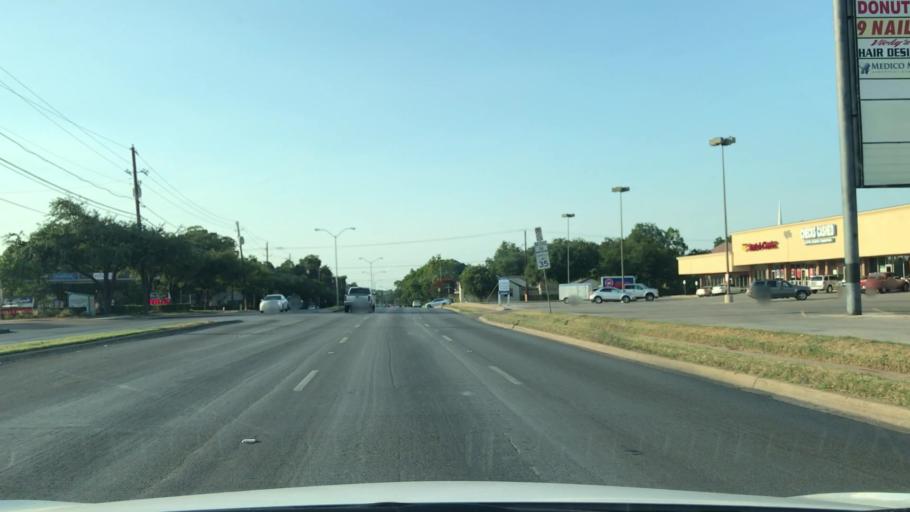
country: US
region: Texas
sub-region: Dallas County
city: Cockrell Hill
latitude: 32.7418
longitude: -96.8567
